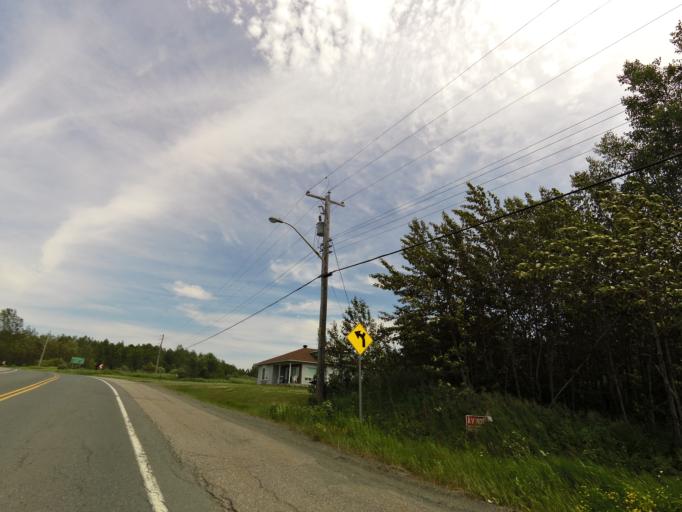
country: CA
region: Quebec
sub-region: Abitibi-Temiscamingue
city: Rouyn-Noranda
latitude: 47.9136
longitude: -79.2434
